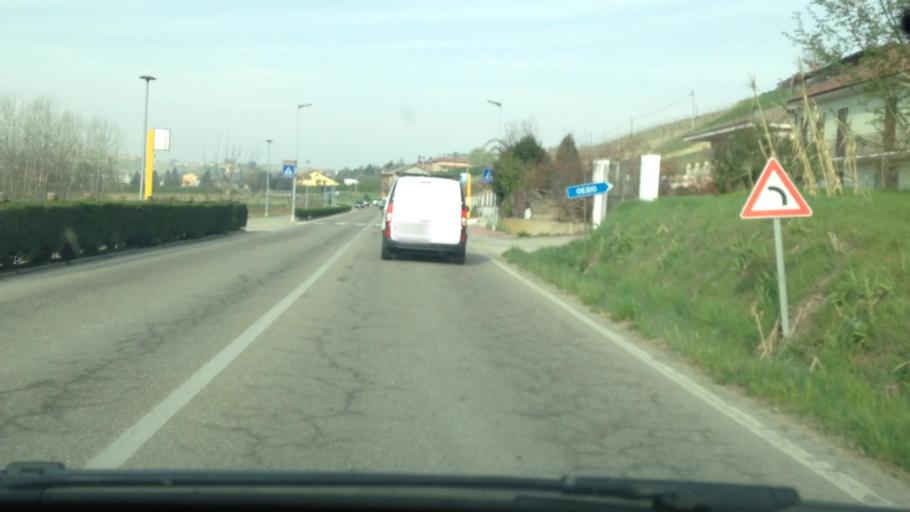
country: IT
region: Piedmont
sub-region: Provincia di Cuneo
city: Canale
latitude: 44.8002
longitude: 8.0131
